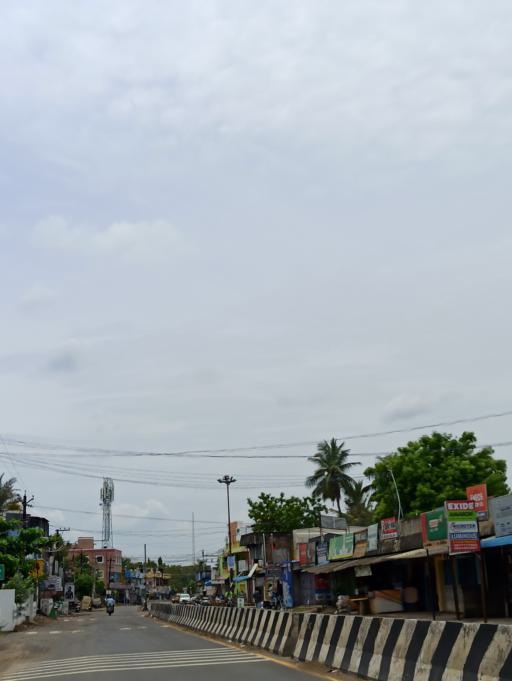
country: IN
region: Tamil Nadu
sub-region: Kancheepuram
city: Vandalur
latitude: 12.9108
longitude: 80.0696
